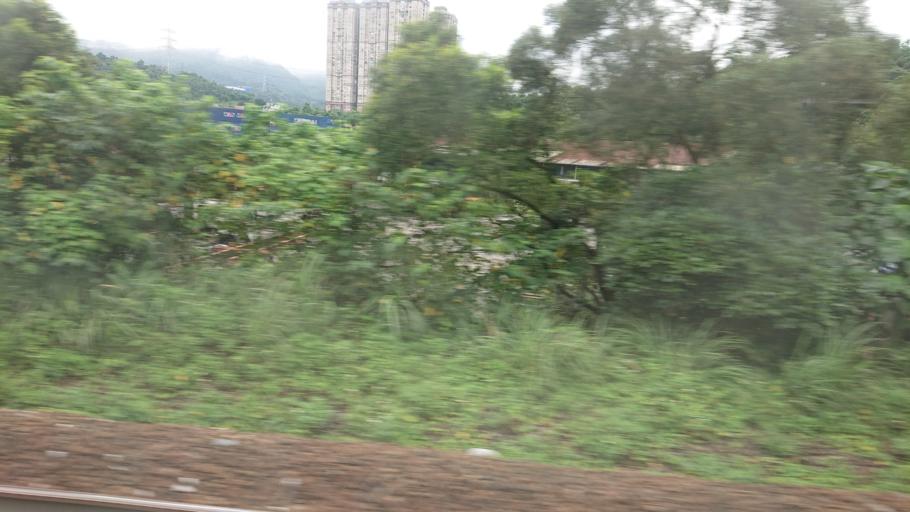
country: TW
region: Taiwan
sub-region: Keelung
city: Keelung
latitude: 25.0806
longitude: 121.6836
